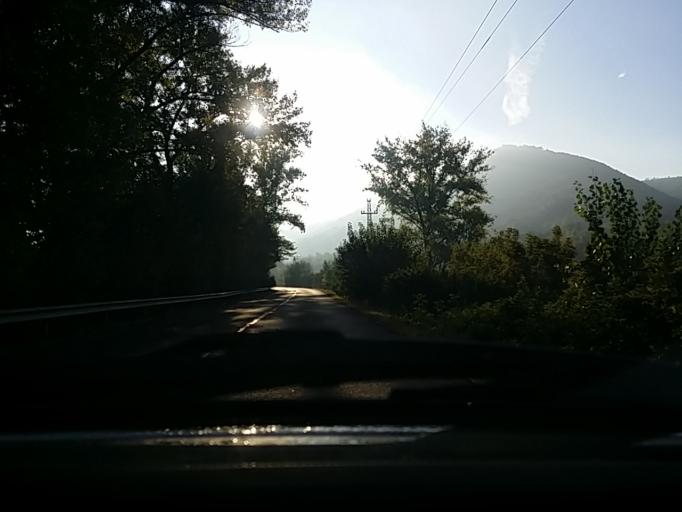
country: HU
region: Pest
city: Nagymaros
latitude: 47.7621
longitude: 18.9263
